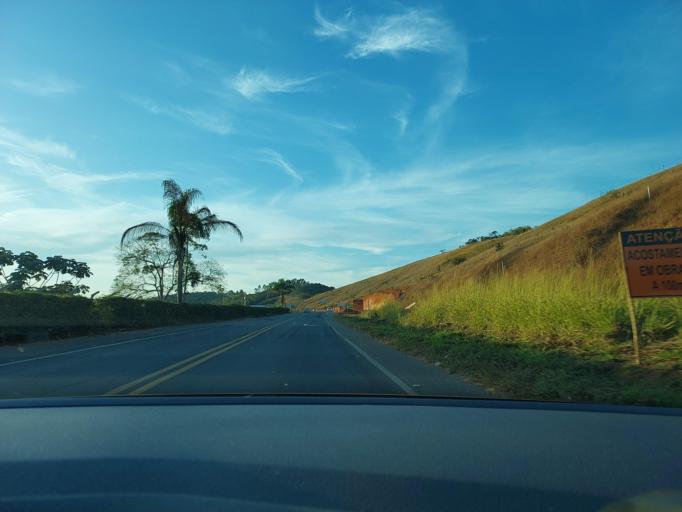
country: BR
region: Minas Gerais
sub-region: Vicosa
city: Vicosa
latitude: -20.7902
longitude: -42.8385
